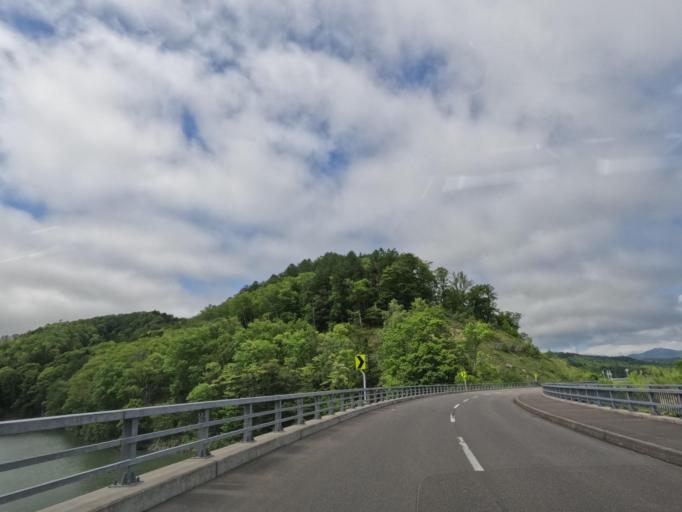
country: JP
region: Hokkaido
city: Tobetsu
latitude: 43.3419
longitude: 141.5642
